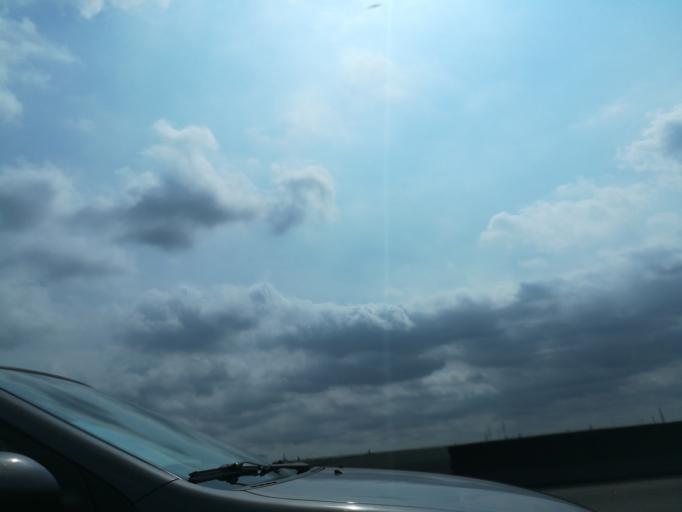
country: NG
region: Lagos
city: Somolu
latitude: 6.5252
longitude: 3.4040
